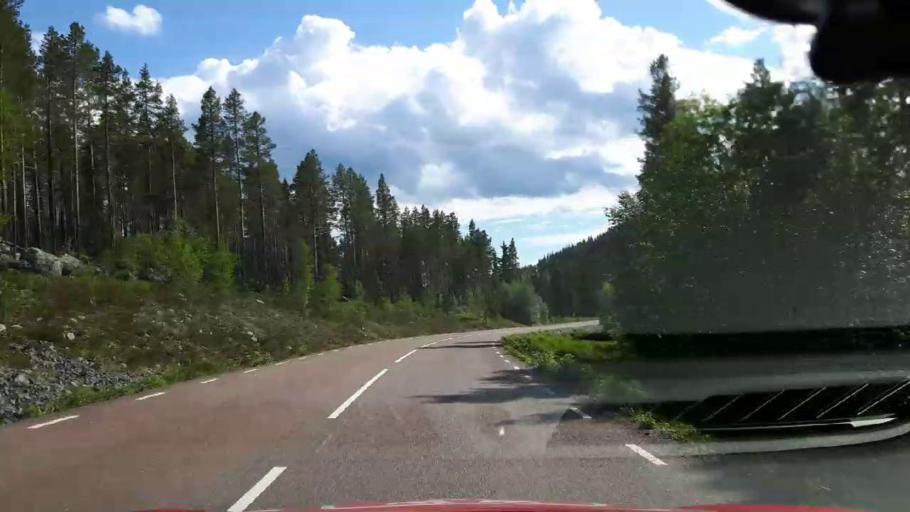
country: SE
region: Jaemtland
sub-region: Krokoms Kommun
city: Valla
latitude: 64.0017
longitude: 14.2392
